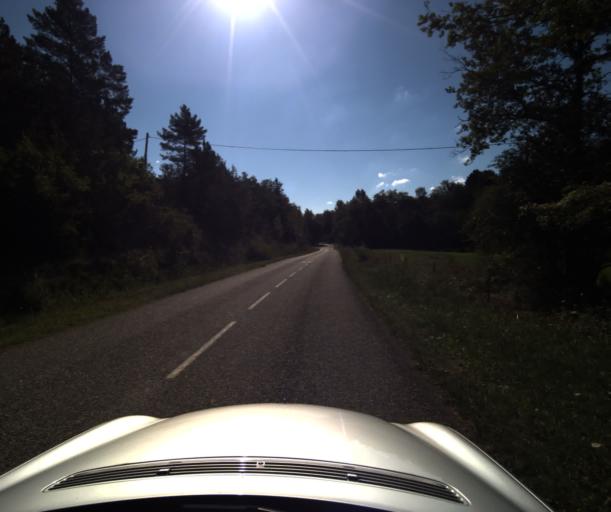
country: FR
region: Languedoc-Roussillon
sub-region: Departement de l'Aude
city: Chalabre
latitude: 42.9695
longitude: 1.9440
